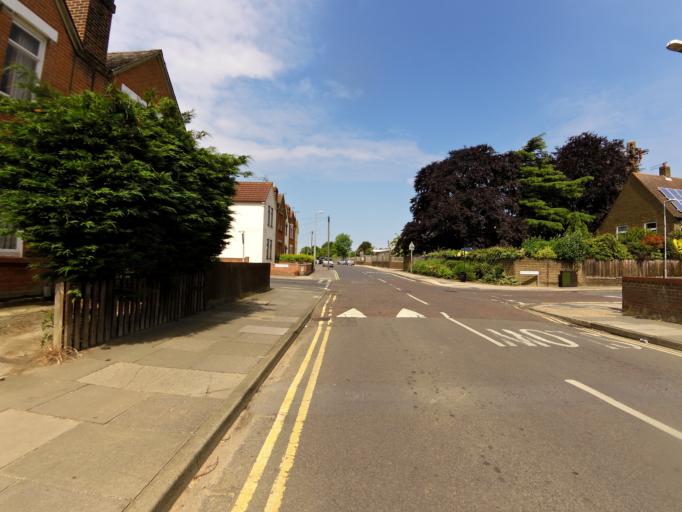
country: GB
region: England
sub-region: Suffolk
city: Ipswich
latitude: 52.0693
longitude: 1.1294
